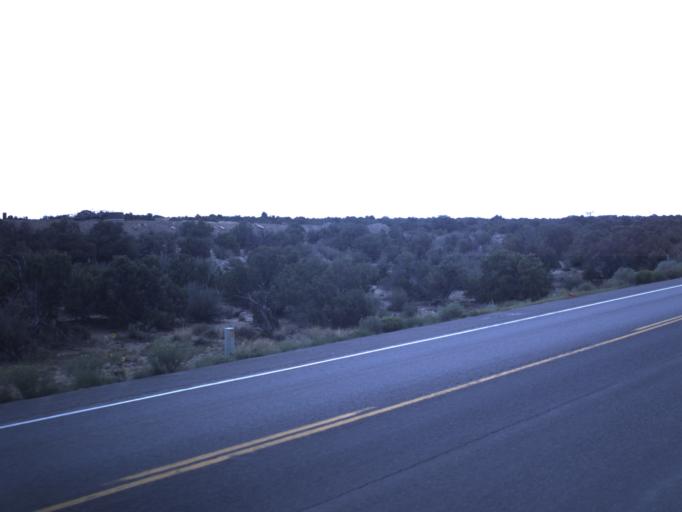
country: US
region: Utah
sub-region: Duchesne County
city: Duchesne
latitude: 40.1642
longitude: -110.4520
